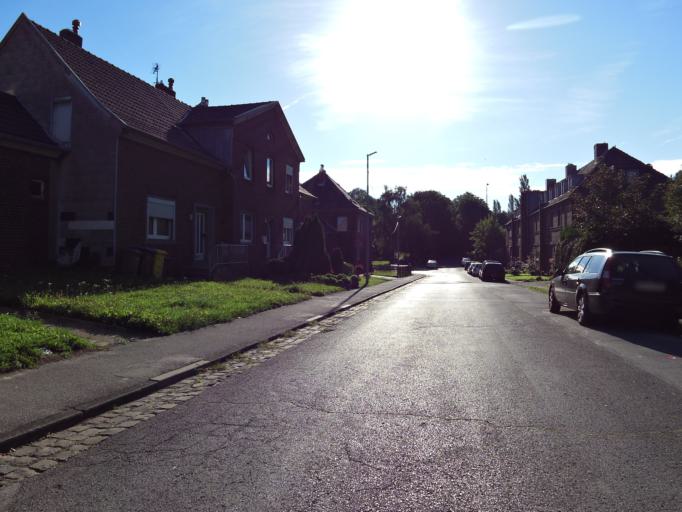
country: DE
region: North Rhine-Westphalia
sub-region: Regierungsbezirk Koln
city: Alsdorf
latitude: 50.8860
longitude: 6.1722
